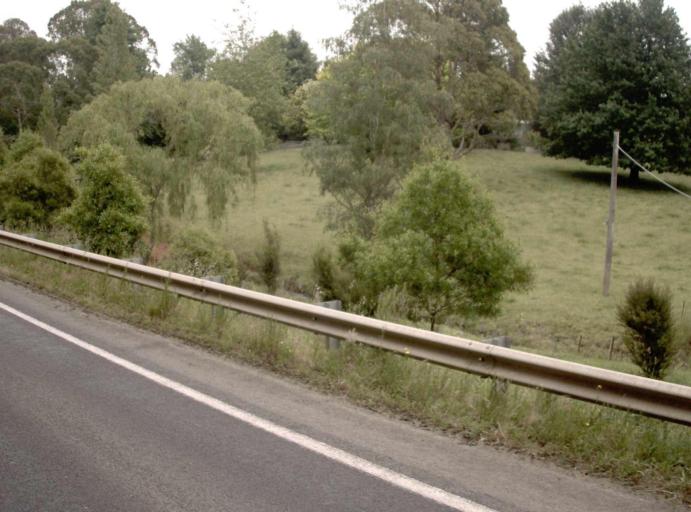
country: AU
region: Victoria
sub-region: Latrobe
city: Moe
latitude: -38.3841
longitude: 146.1731
